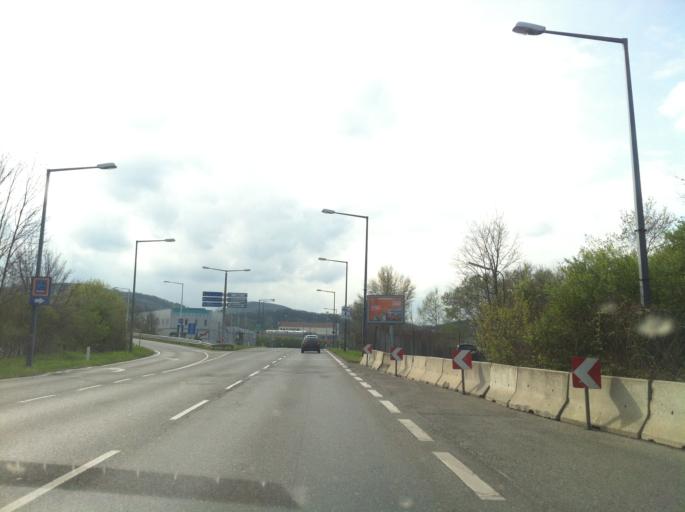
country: AT
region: Lower Austria
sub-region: Politischer Bezirk Wien-Umgebung
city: Purkersdorf
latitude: 48.2058
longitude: 16.2273
